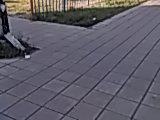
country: RU
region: Orenburg
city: Novotroitsk
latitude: 51.1936
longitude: 58.2946
